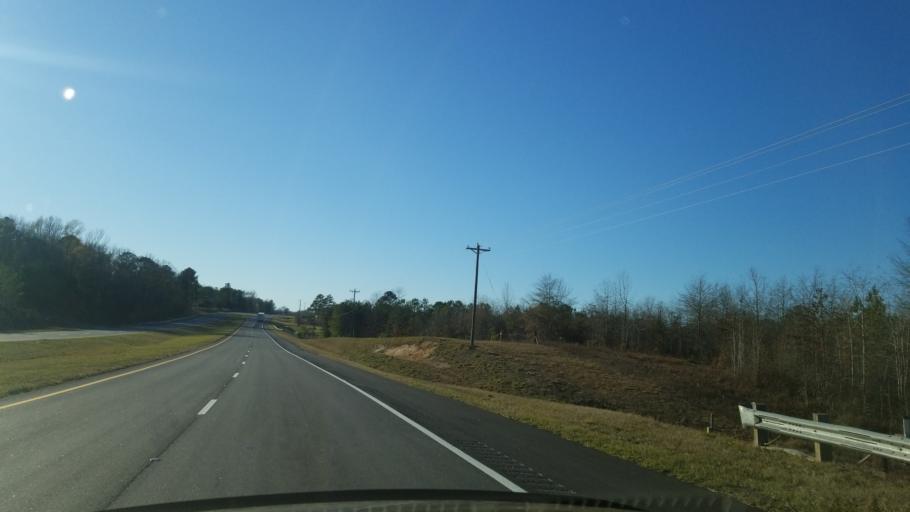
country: US
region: Georgia
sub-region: Talbot County
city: Talbotton
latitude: 32.5756
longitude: -84.5716
